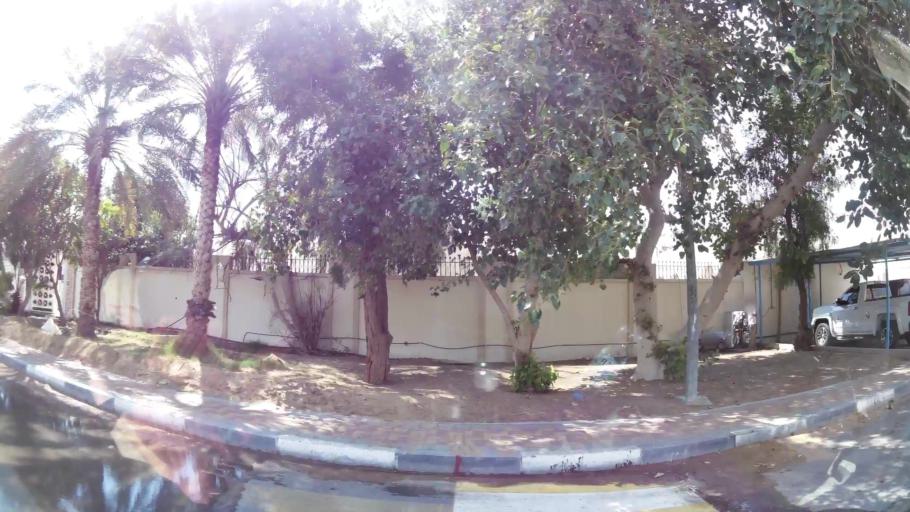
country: AE
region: Abu Dhabi
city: Al Ain
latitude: 24.1894
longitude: 55.7940
